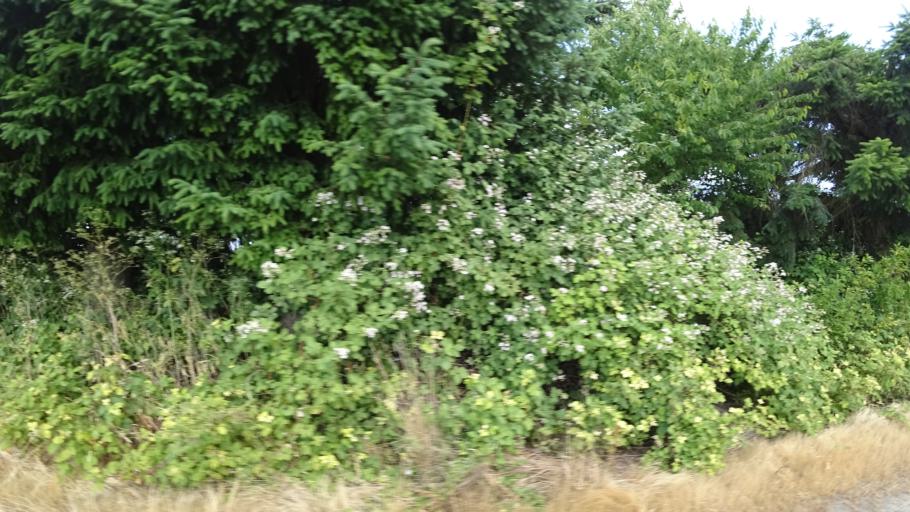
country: US
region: Washington
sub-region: Clark County
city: Felida
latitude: 45.6566
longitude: -122.7793
